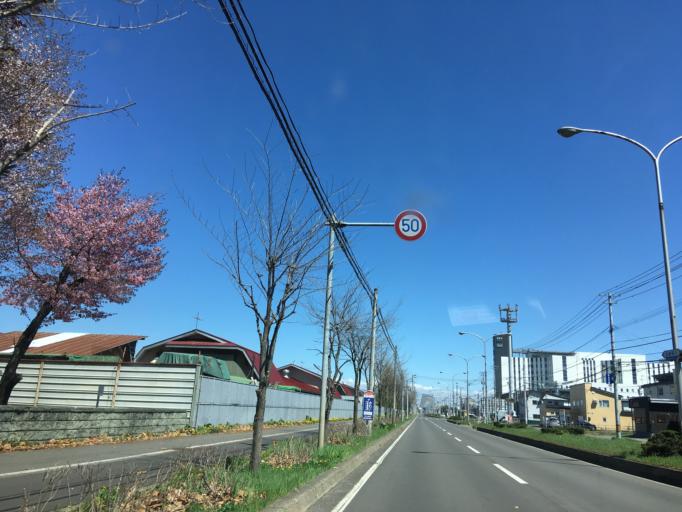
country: JP
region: Hokkaido
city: Obihiro
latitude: 42.9201
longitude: 143.1760
